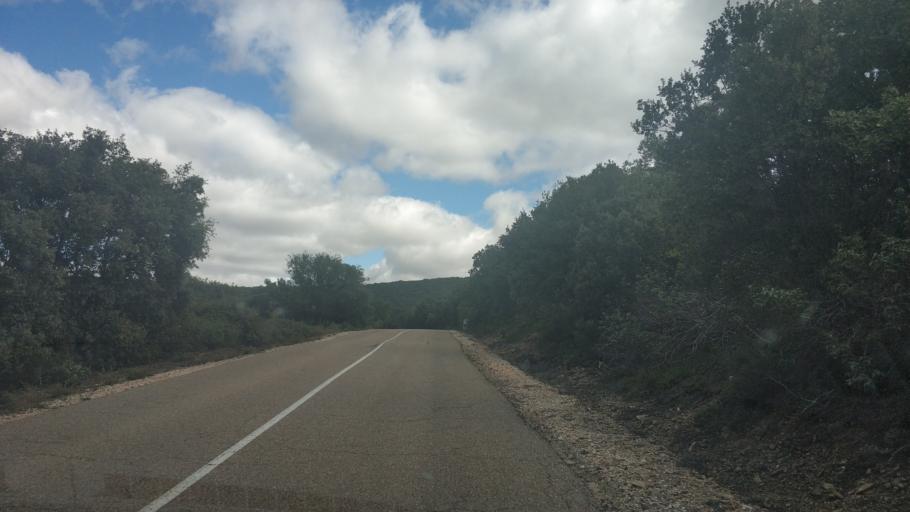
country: ES
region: Castille and Leon
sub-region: Provincia de Burgos
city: Retuerta
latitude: 42.0426
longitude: -3.4947
